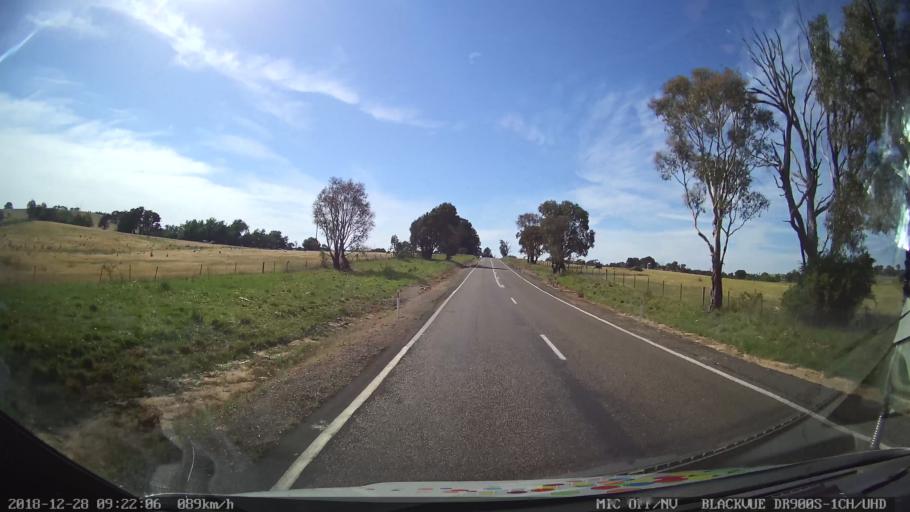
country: AU
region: New South Wales
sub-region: Upper Lachlan Shire
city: Crookwell
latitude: -34.3700
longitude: 149.3790
